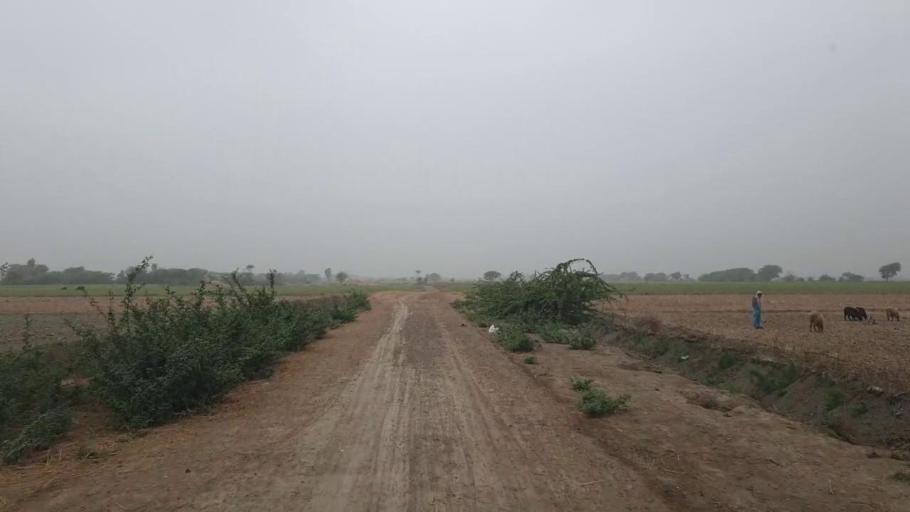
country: PK
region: Sindh
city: Badin
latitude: 24.5692
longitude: 68.6487
